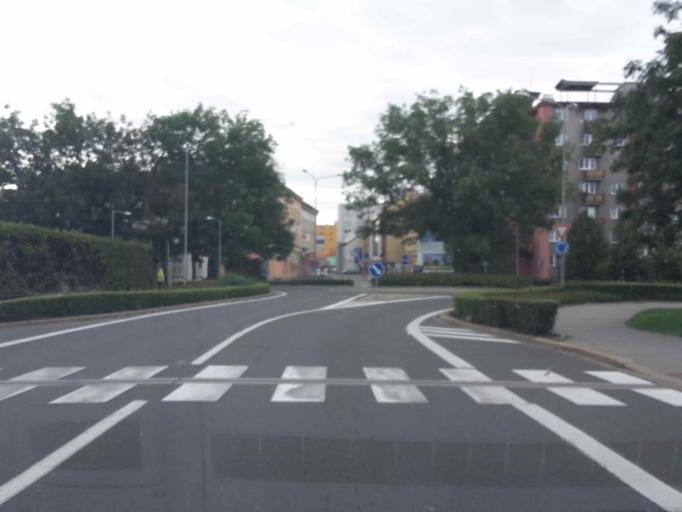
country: CZ
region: Olomoucky
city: Prerov
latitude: 49.4557
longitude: 17.4461
